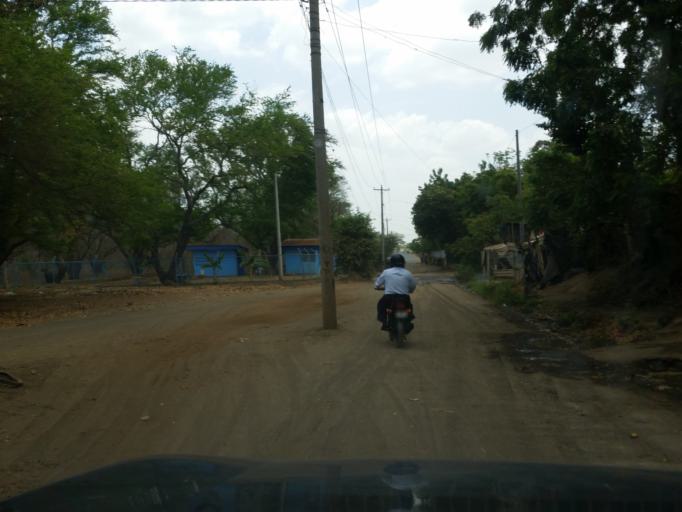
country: NI
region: Managua
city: Managua
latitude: 12.1369
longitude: -86.1868
